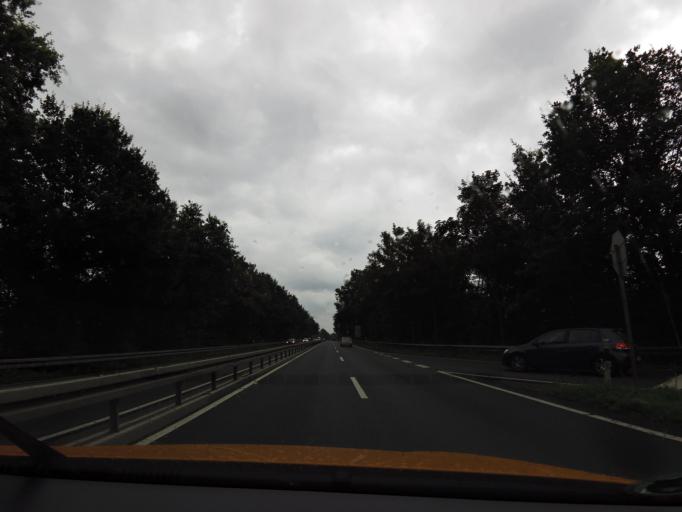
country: DE
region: Lower Saxony
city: Neustadt am Rubenberge
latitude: 52.5133
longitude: 9.4630
